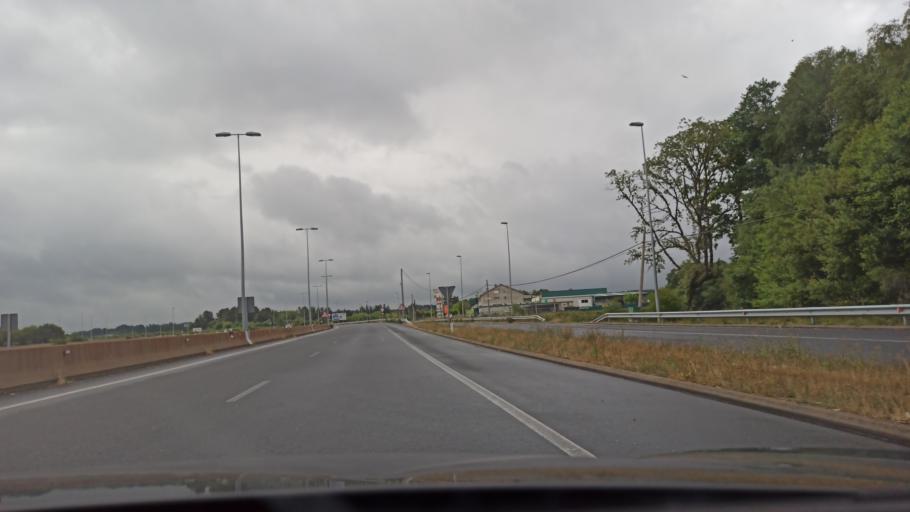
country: ES
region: Galicia
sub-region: Provincia de Lugo
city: Lugo
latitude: 42.9839
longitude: -7.5878
